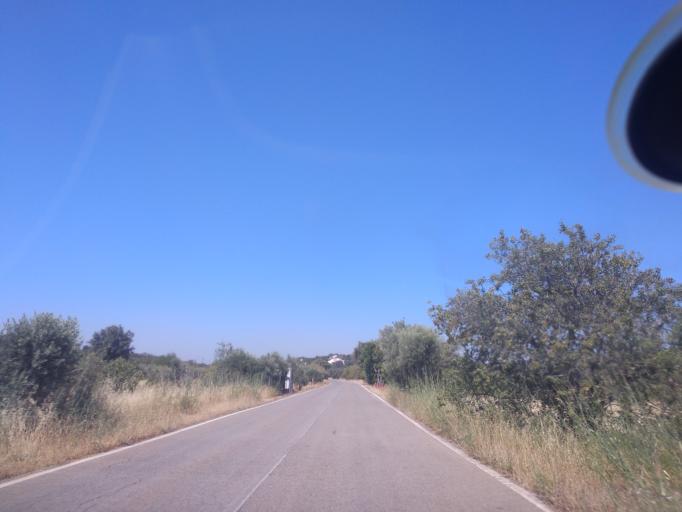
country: PT
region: Faro
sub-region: Sao Bras de Alportel
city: Sao Bras de Alportel
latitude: 37.1628
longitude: -7.9288
